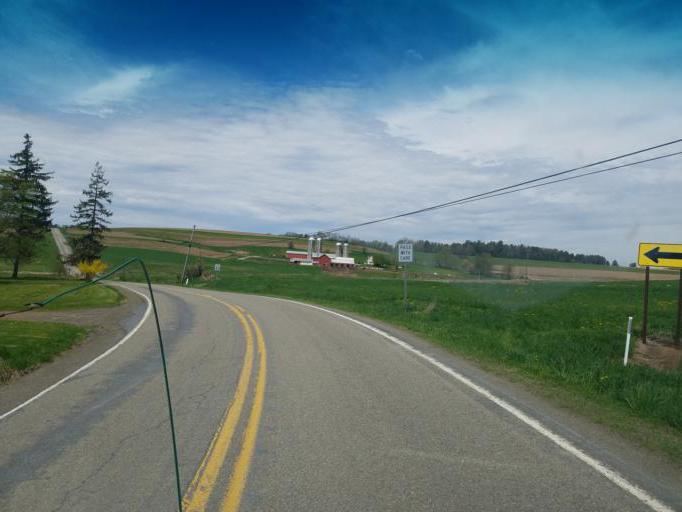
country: US
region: Pennsylvania
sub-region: Tioga County
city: Wellsboro
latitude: 41.7050
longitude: -77.3999
